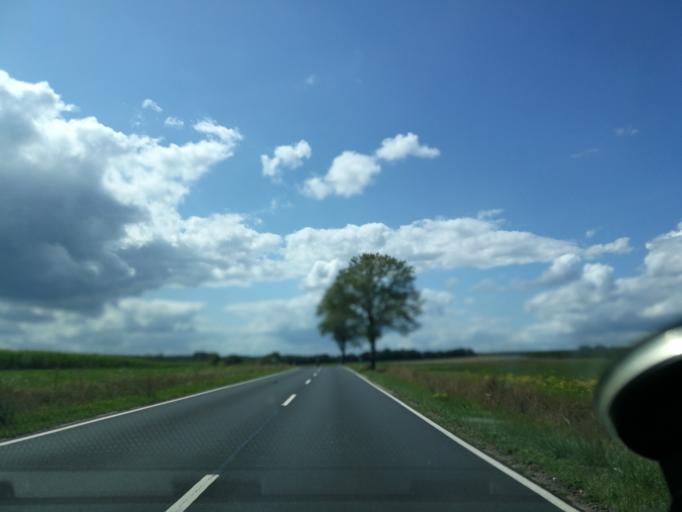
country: DE
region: Rheinland-Pfalz
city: Herforst
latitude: 49.9621
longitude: 6.6960
